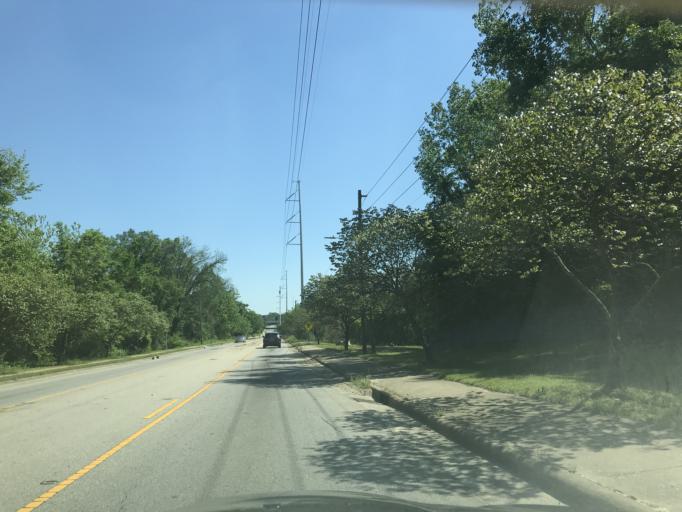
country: US
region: North Carolina
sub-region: Wake County
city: Raleigh
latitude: 35.7596
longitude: -78.6315
